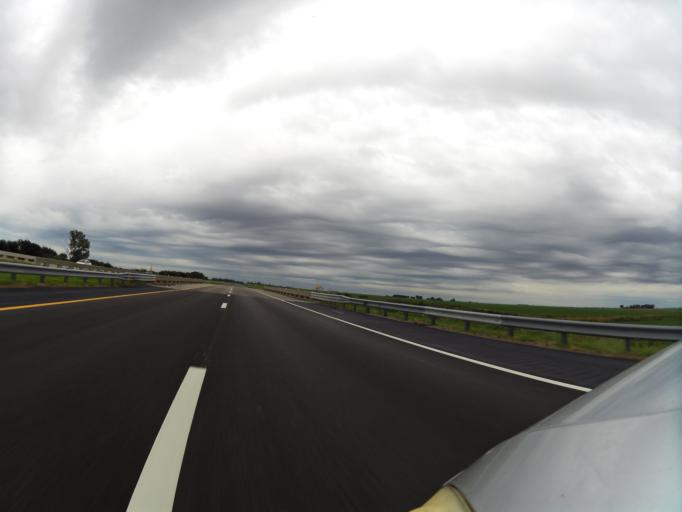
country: US
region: Kansas
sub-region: Sedgwick County
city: Colwich
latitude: 37.8377
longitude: -97.5709
